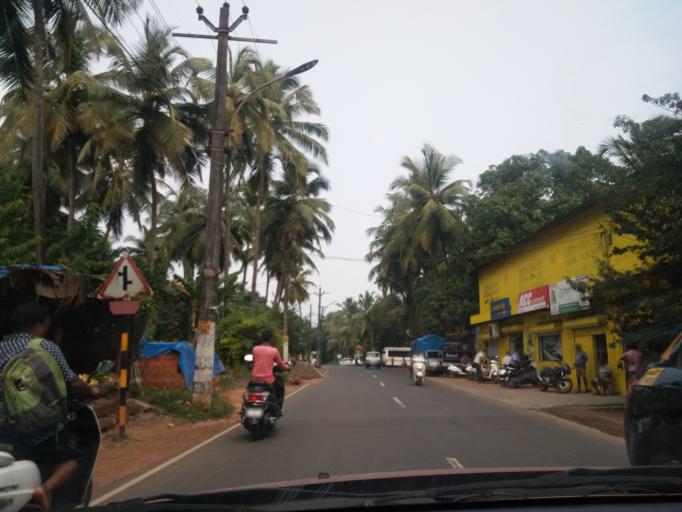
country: IN
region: Goa
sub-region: North Goa
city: Goa Velha
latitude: 15.4321
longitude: 73.8972
